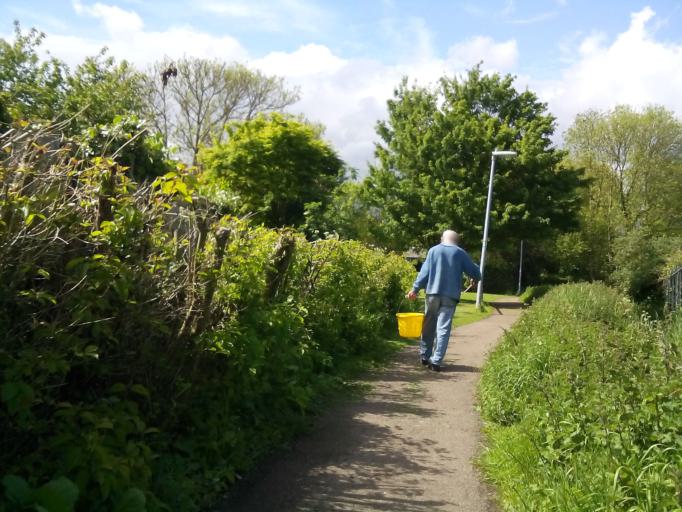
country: GB
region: England
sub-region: Cambridgeshire
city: Cambridge
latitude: 52.1890
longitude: 0.1673
